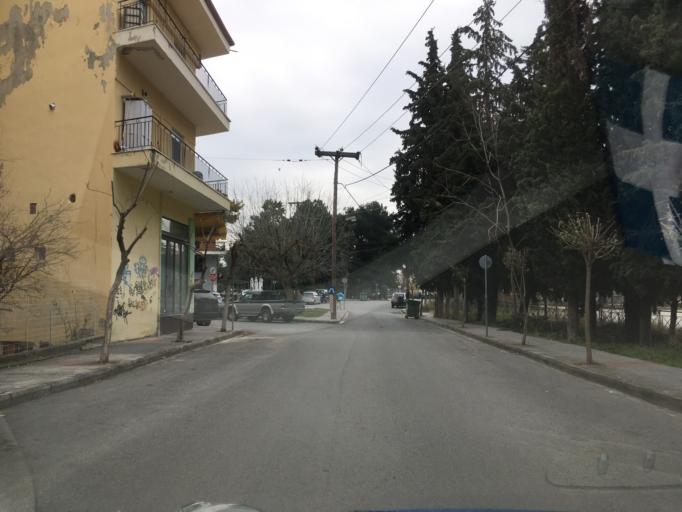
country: GR
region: West Macedonia
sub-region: Nomos Kozanis
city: Kozani
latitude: 40.2953
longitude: 21.7914
